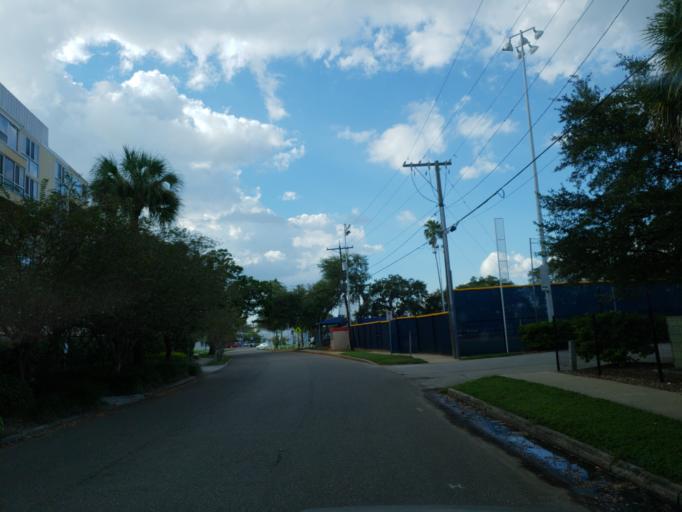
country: US
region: Florida
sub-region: Hillsborough County
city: Tampa
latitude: 27.9288
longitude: -82.4536
